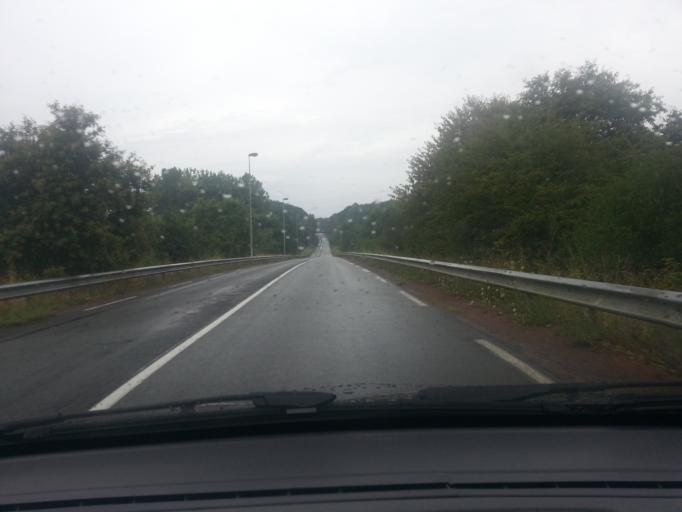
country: FR
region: Bourgogne
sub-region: Departement de Saone-et-Loire
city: Montchanin
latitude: 46.7583
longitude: 4.4941
